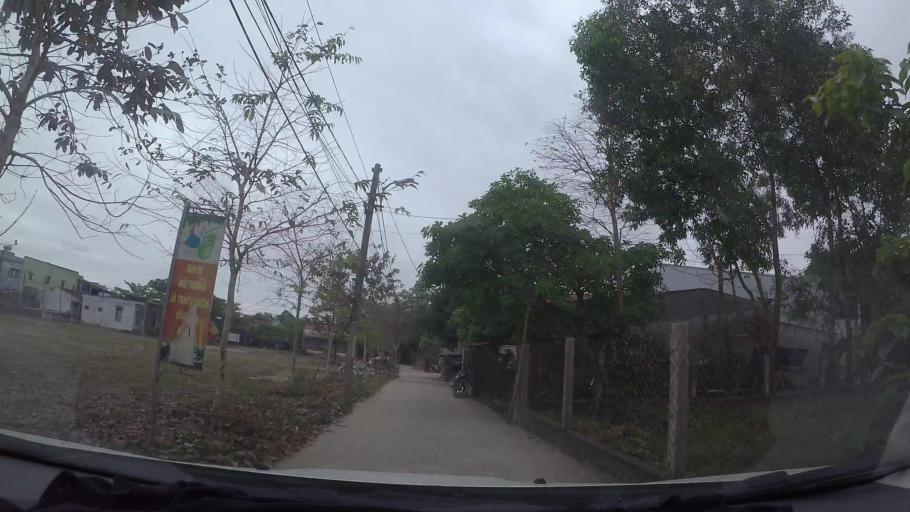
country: VN
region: Da Nang
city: Lien Chieu
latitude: 16.0767
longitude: 108.0983
